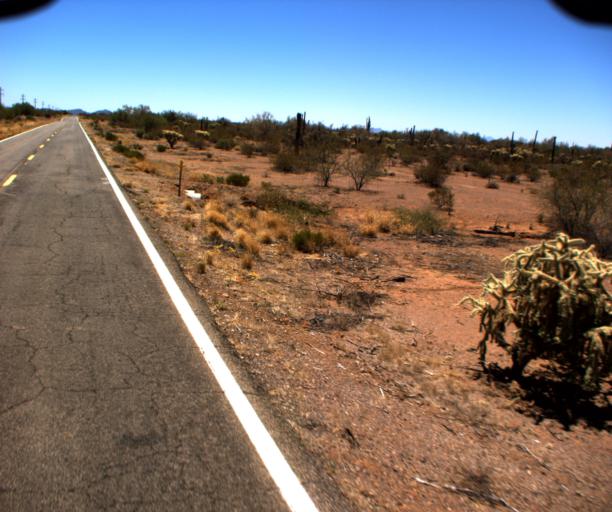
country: US
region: Arizona
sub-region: Pima County
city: Sells
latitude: 32.0778
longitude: -112.0477
